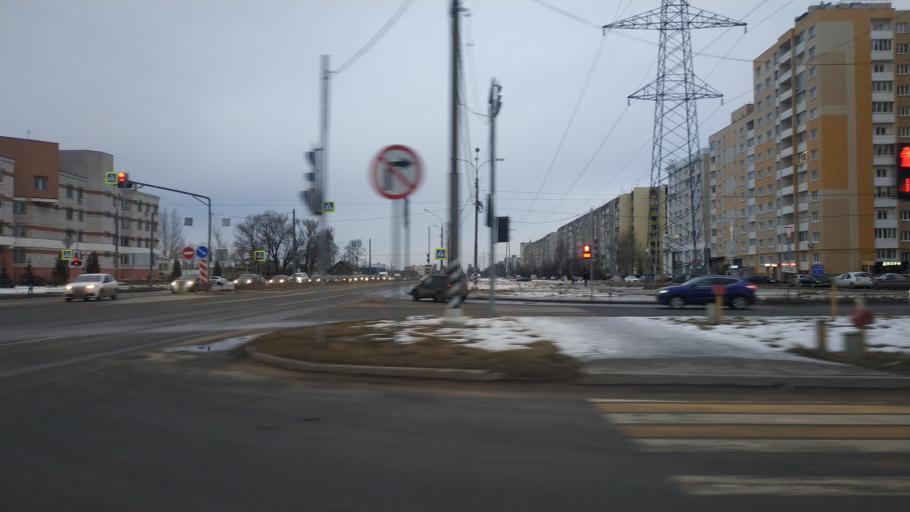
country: RU
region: Tverskaya
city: Tver
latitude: 56.8179
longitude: 35.8845
